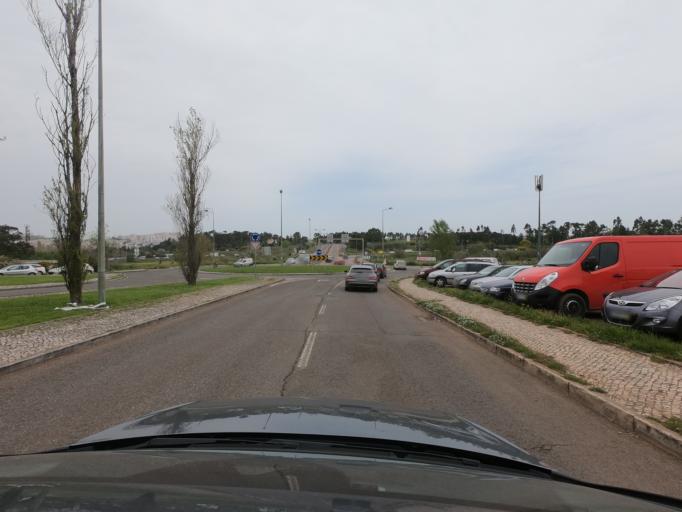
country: PT
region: Lisbon
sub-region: Sintra
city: Queluz
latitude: 38.7464
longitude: -9.2463
